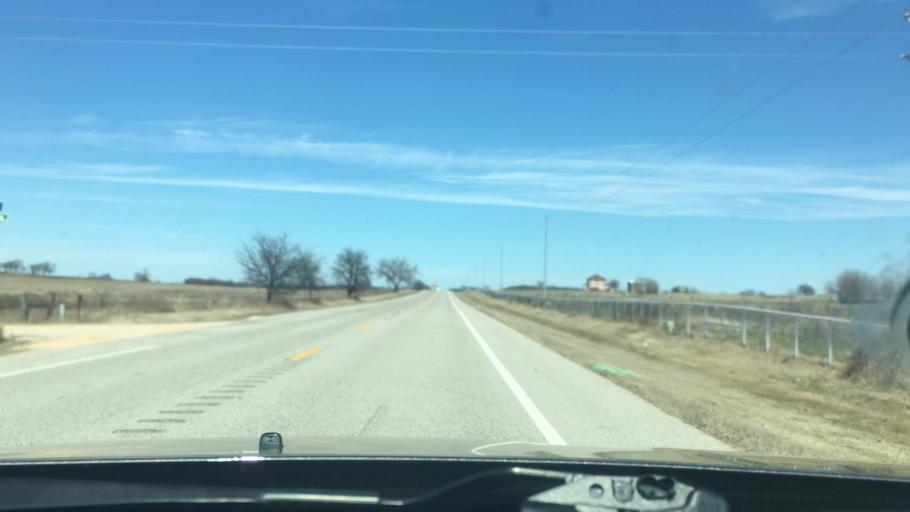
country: US
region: Oklahoma
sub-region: Murray County
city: Sulphur
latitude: 34.3757
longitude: -96.9508
